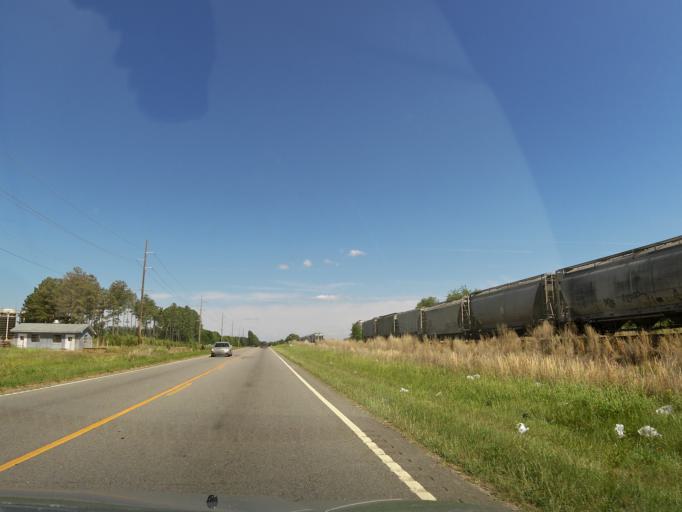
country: US
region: South Carolina
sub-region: Aiken County
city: Aiken
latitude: 33.5428
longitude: -81.6710
